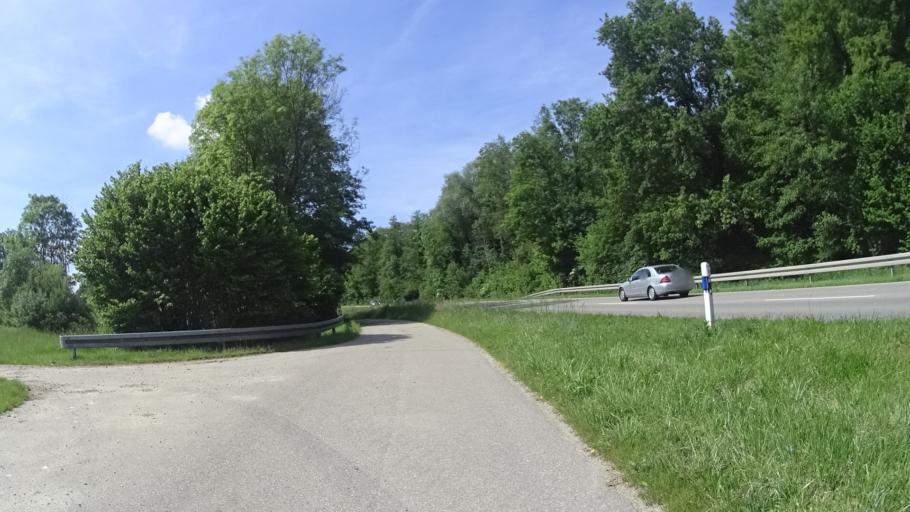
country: DE
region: Baden-Wuerttemberg
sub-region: Freiburg Region
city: Schutterwald
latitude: 48.4898
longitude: 7.8188
